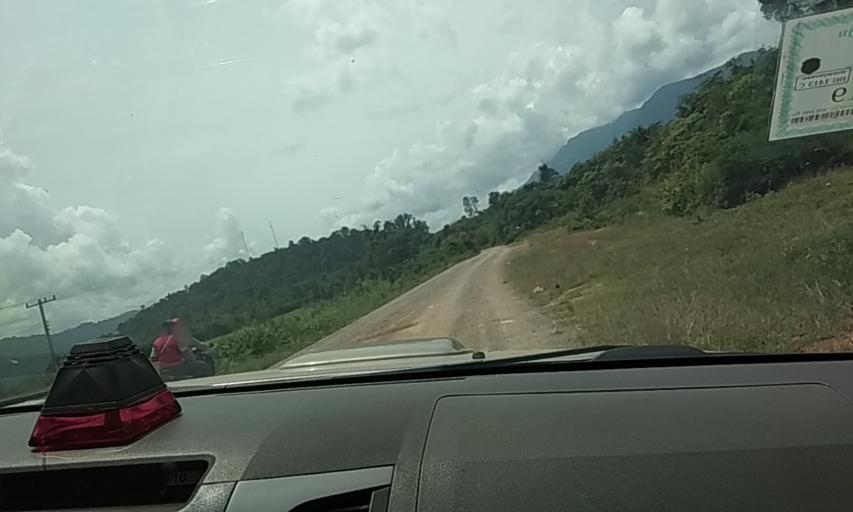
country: LA
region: Bolikhamxai
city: Ban Nahin
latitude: 18.1507
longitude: 104.7337
